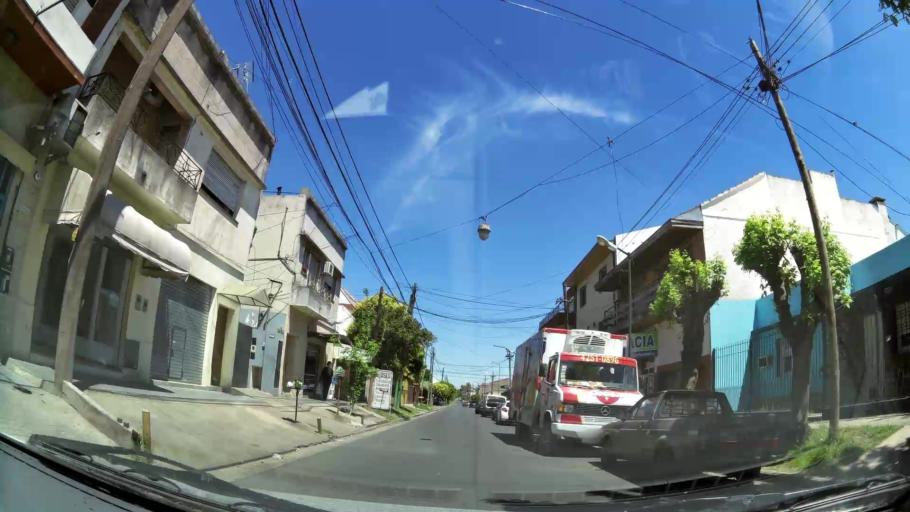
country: AR
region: Buenos Aires
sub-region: Partido de Quilmes
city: Quilmes
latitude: -34.7224
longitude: -58.3062
